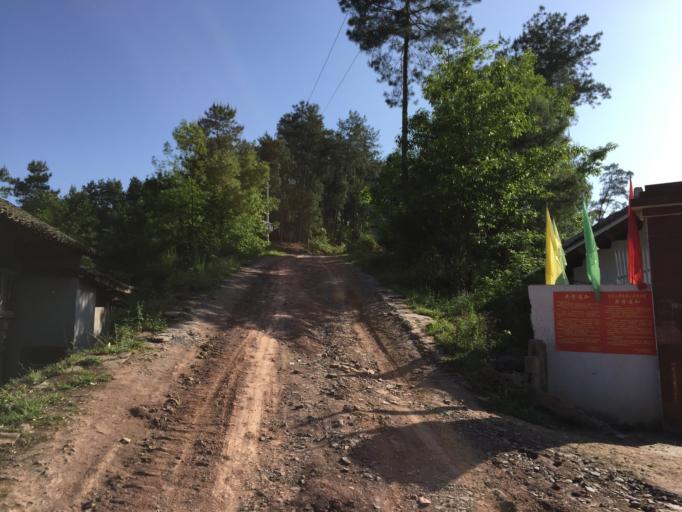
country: CN
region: Guizhou Sheng
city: Xujiaba
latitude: 27.7189
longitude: 108.0225
